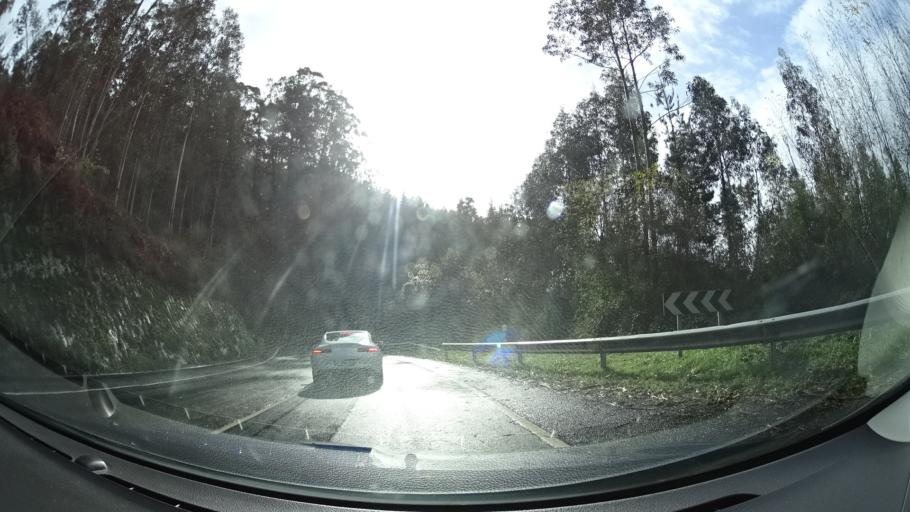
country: ES
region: Basque Country
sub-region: Bizkaia
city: Bakio
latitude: 43.3834
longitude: -2.7888
